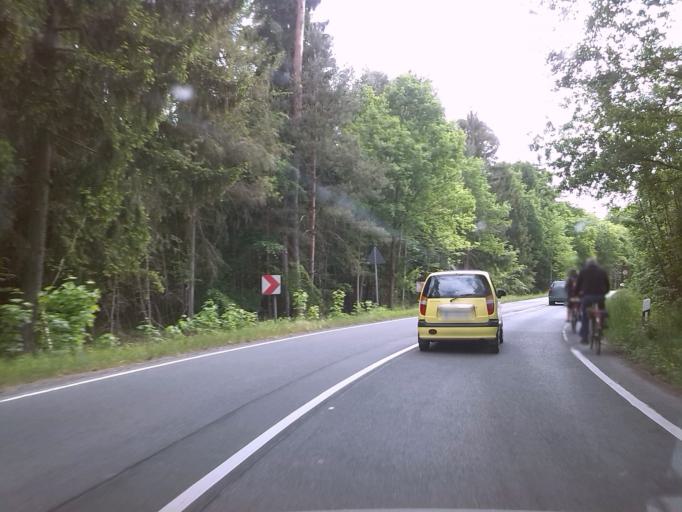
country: DE
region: Hesse
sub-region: Regierungsbezirk Darmstadt
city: Gross-Zimmern
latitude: 49.8858
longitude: 8.8099
